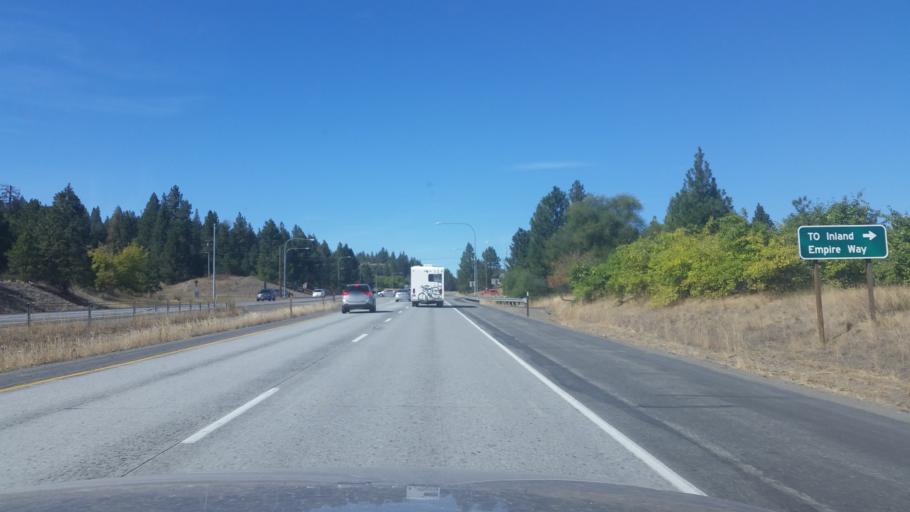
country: US
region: Washington
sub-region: Spokane County
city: Spokane
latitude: 47.6311
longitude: -117.4437
